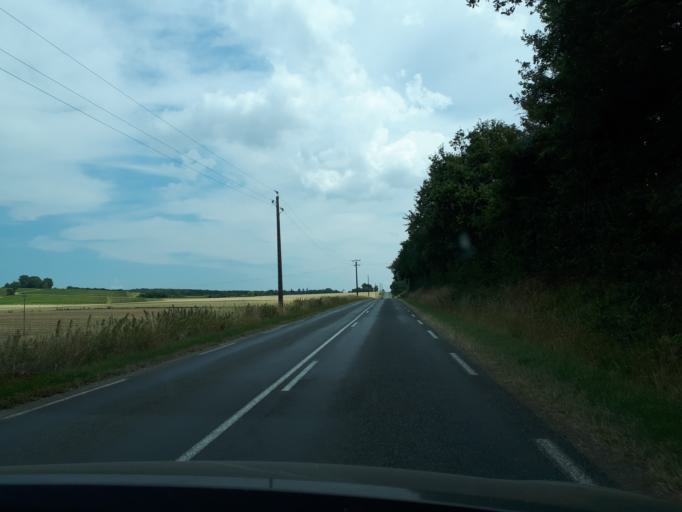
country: FR
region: Centre
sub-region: Departement du Cher
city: Rians
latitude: 47.2149
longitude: 2.6164
